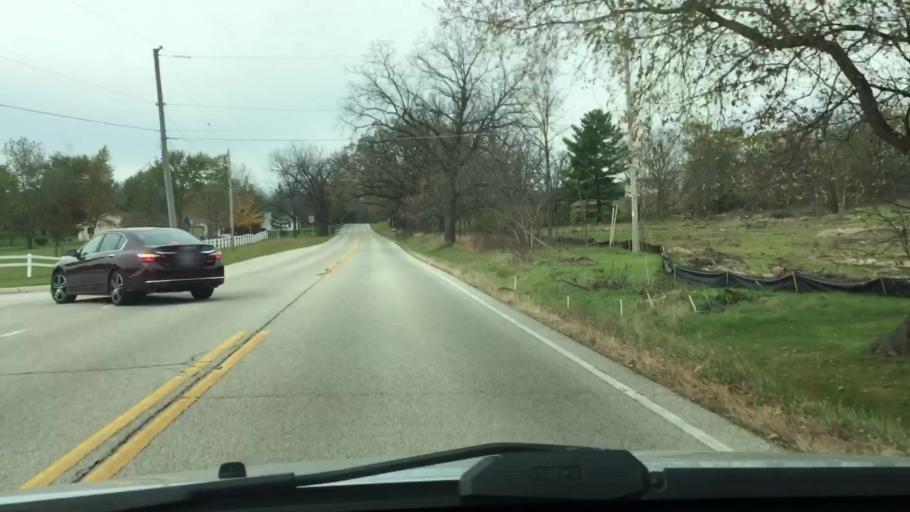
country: US
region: Wisconsin
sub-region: Waukesha County
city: North Prairie
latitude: 42.8974
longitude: -88.3959
